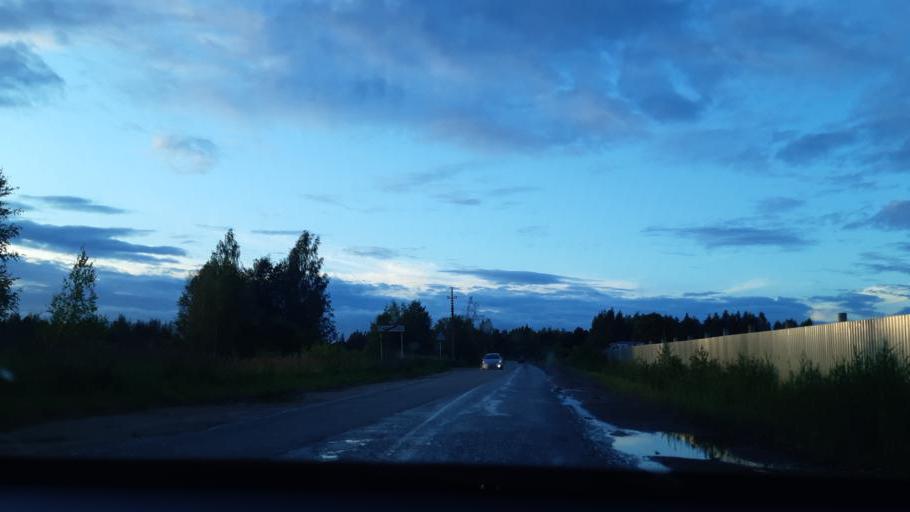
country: RU
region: Smolensk
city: Safonovo
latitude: 55.1274
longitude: 33.2002
